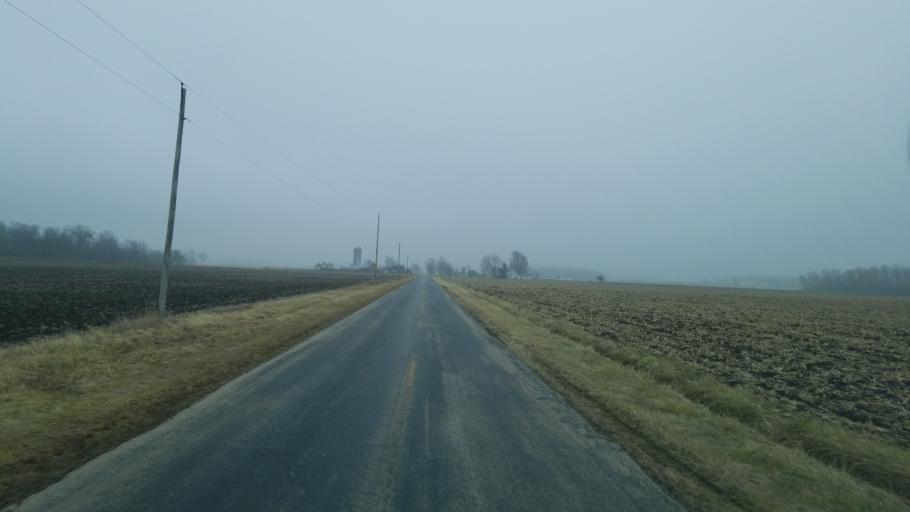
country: US
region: Indiana
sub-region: Adams County
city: Geneva
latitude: 40.6118
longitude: -85.0838
